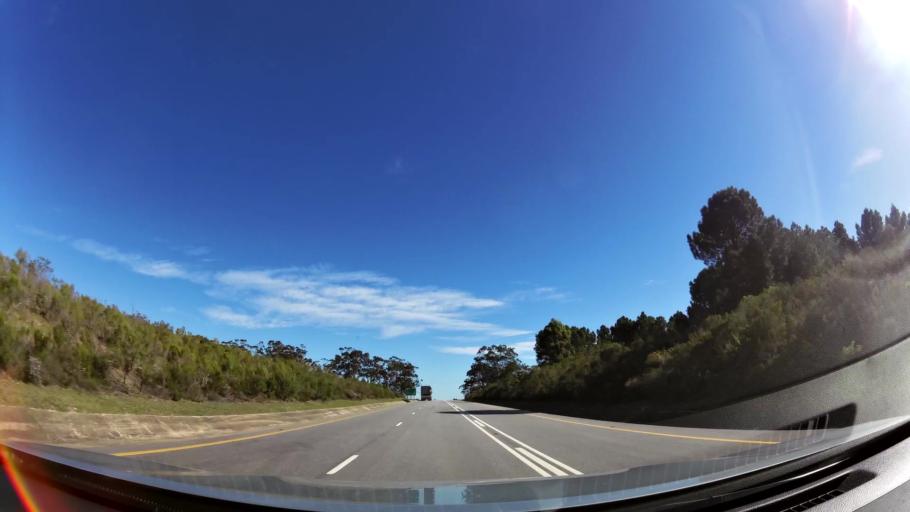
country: ZA
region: Eastern Cape
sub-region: Cacadu District Municipality
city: Kruisfontein
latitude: -34.0195
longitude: 24.6196
